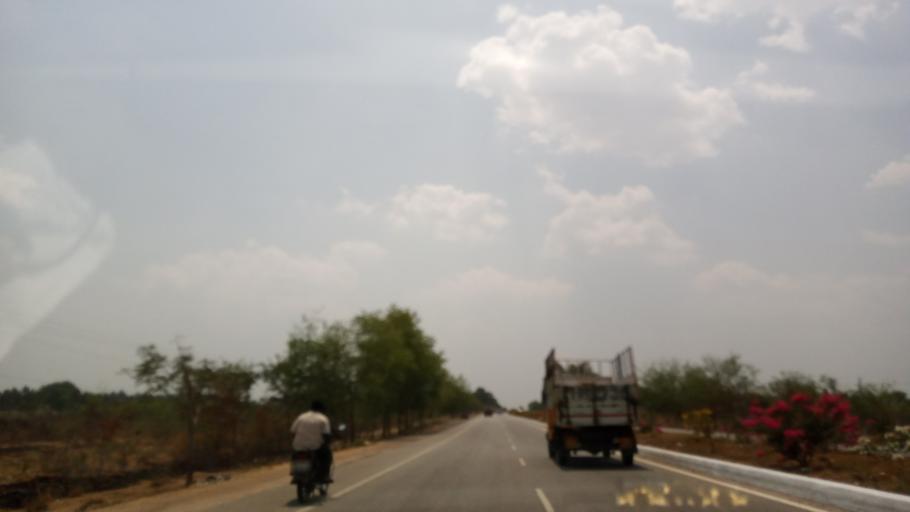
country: IN
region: Karnataka
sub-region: Mandya
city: Belluru
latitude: 12.9726
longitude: 76.8198
